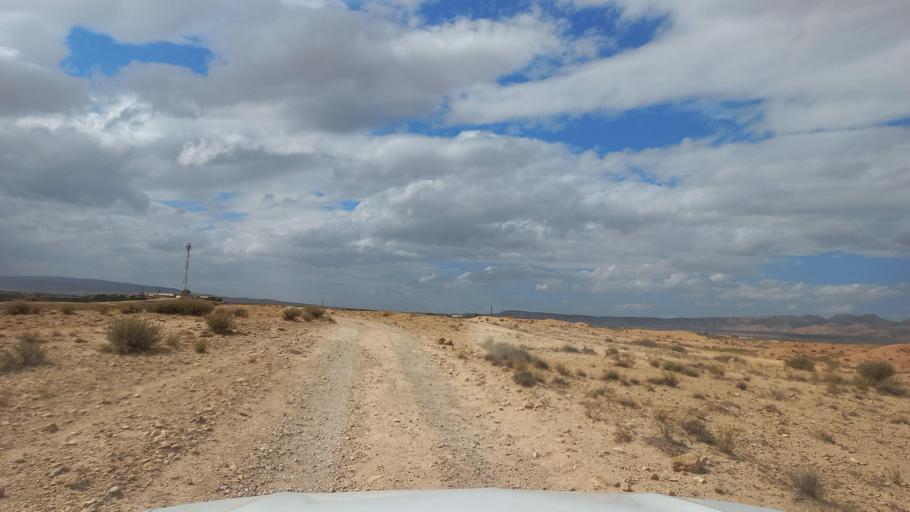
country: TN
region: Al Qasrayn
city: Sbiba
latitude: 35.3789
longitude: 9.1024
